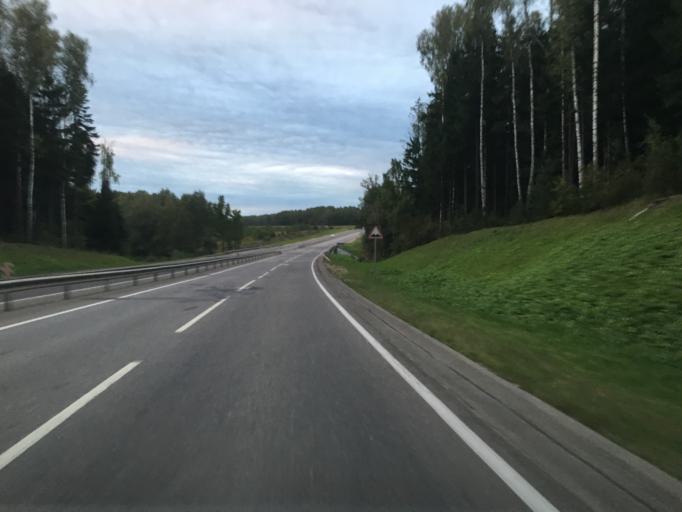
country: RU
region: Kaluga
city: Kaluga
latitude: 54.6615
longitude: 36.2857
